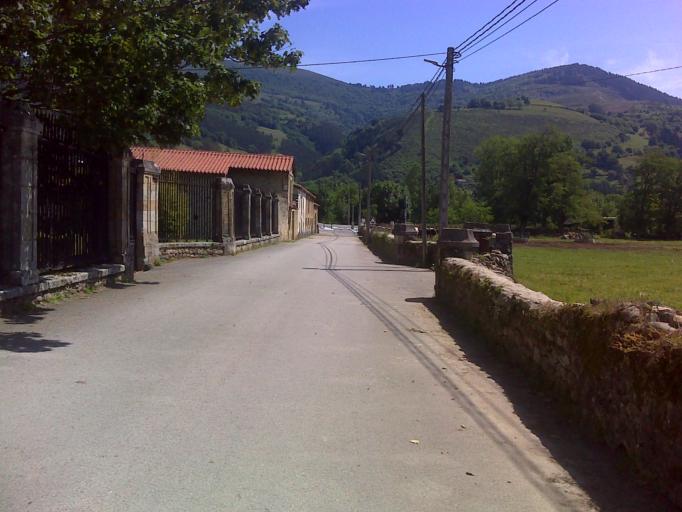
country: ES
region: Cantabria
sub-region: Provincia de Cantabria
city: Santiurde de Toranzo
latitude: 43.2030
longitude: -3.9269
